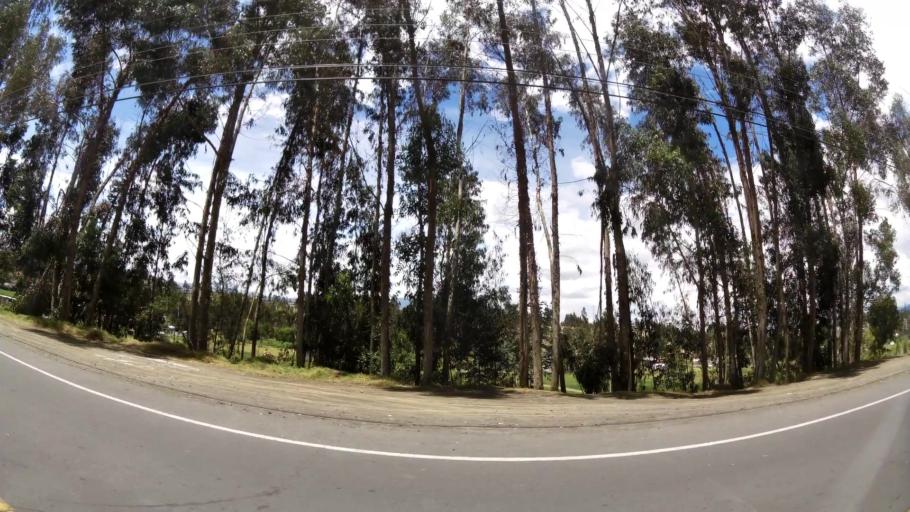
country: EC
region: Tungurahua
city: Ambato
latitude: -1.2815
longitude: -78.5937
